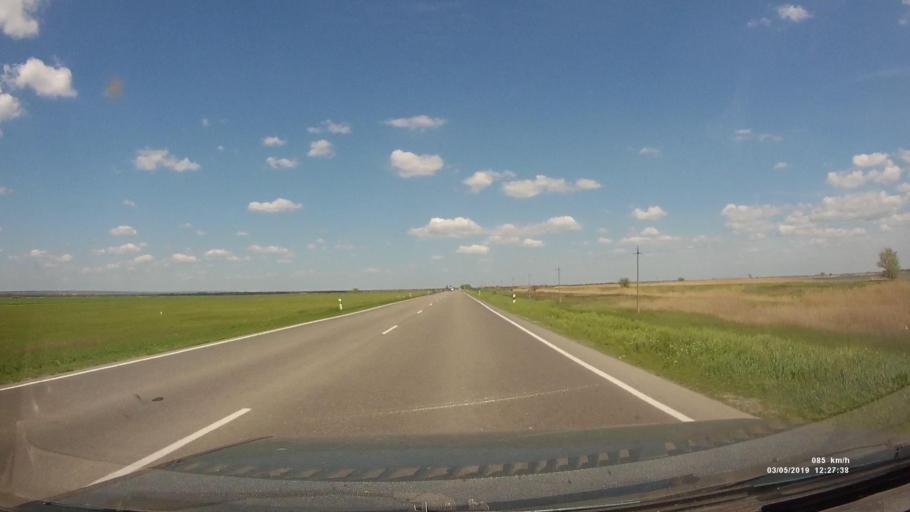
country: RU
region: Rostov
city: Semikarakorsk
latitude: 47.4617
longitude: 40.7223
